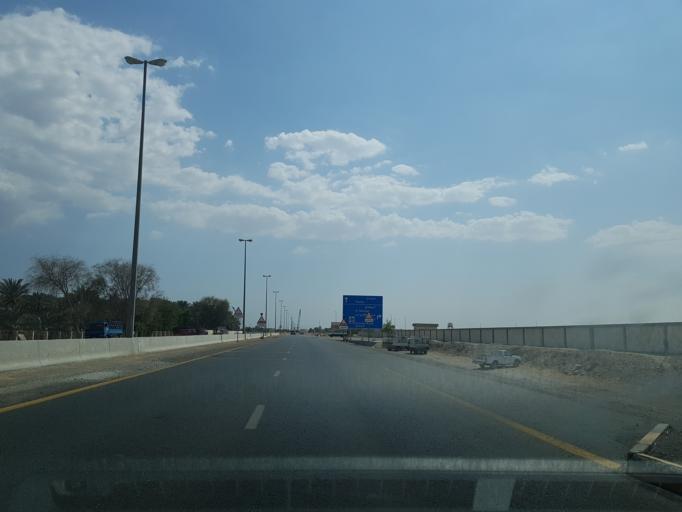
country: AE
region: Ash Shariqah
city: Adh Dhayd
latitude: 25.2360
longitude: 55.9165
